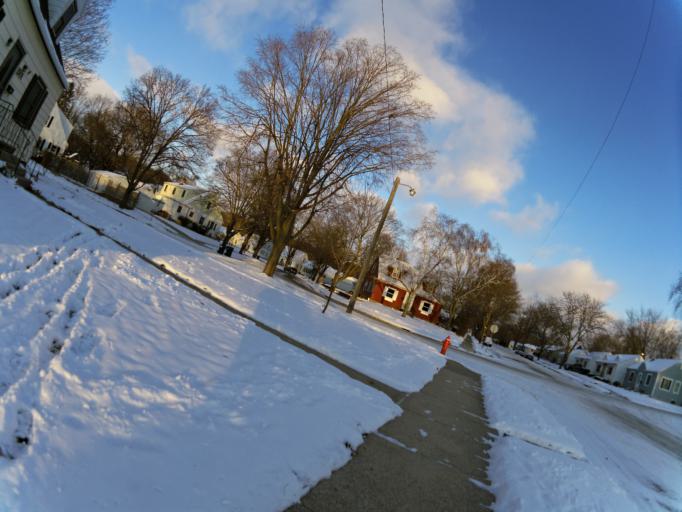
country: US
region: Minnesota
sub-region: Olmsted County
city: Rochester
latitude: 44.0371
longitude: -92.4542
